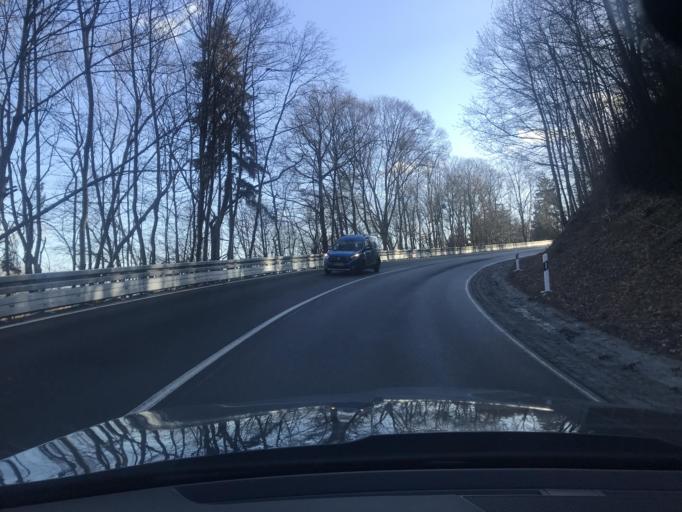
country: DE
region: Saxony-Anhalt
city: Blankenburg
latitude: 51.7911
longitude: 10.9364
